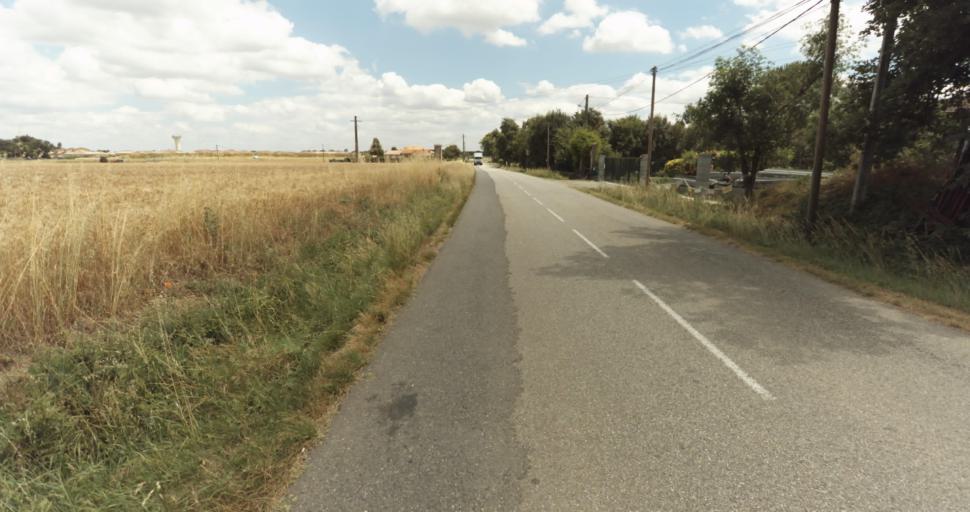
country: FR
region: Midi-Pyrenees
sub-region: Departement de la Haute-Garonne
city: Fontenilles
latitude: 43.5461
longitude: 1.1839
